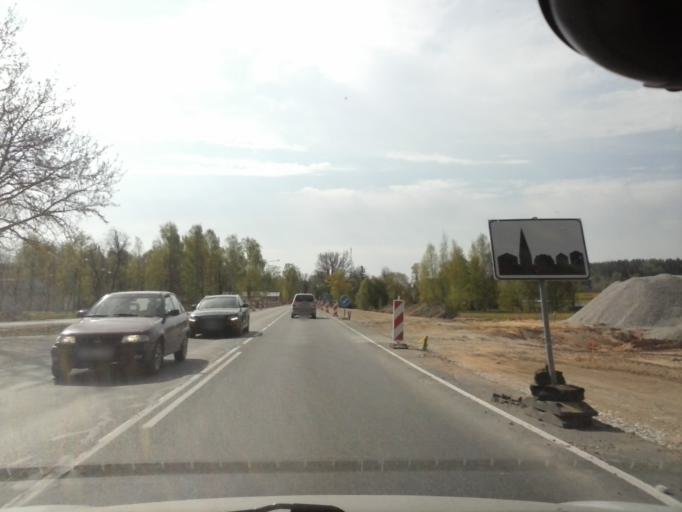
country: EE
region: Tartu
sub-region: UElenurme vald
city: Ulenurme
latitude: 58.2377
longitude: 26.6905
